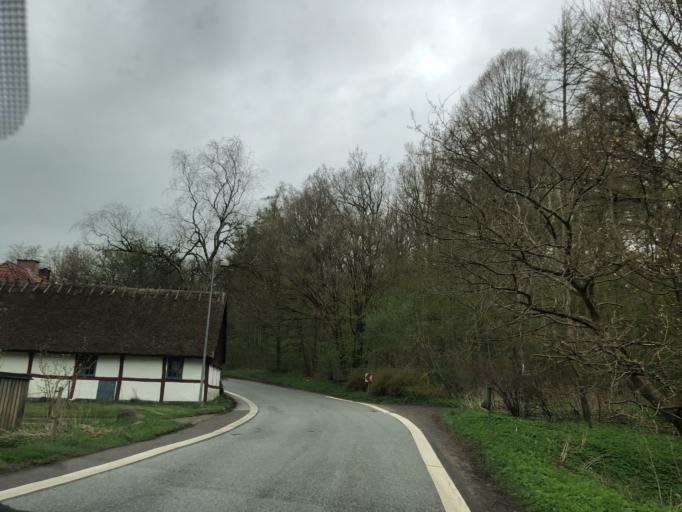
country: DK
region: Zealand
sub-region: Lejre Kommune
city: Kirke Hvalso
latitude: 55.5255
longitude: 11.8608
